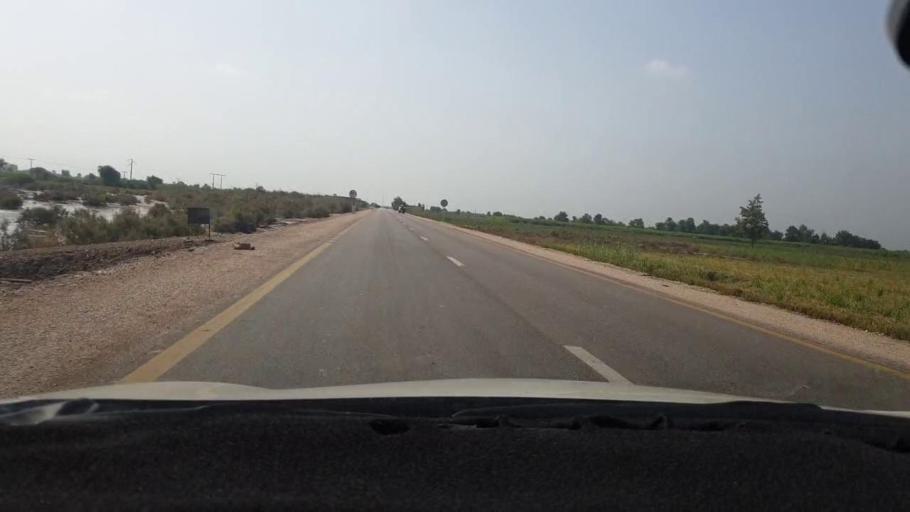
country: PK
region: Sindh
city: Jhol
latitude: 25.8531
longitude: 69.0603
